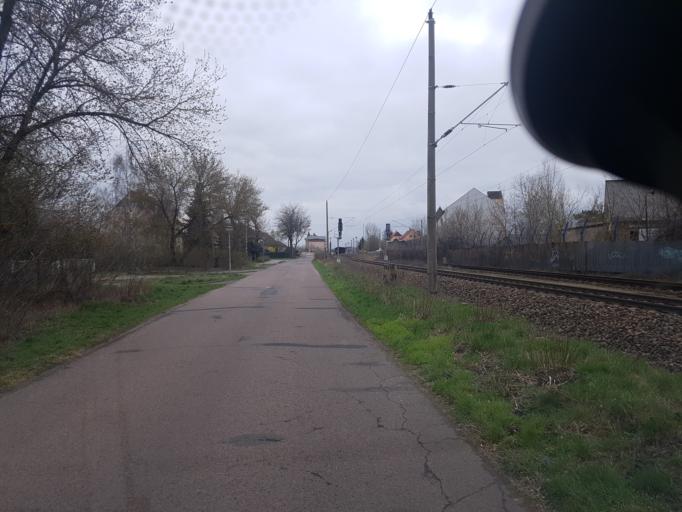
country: DE
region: Brandenburg
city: Eisenhuettenstadt
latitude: 52.1514
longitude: 14.6591
